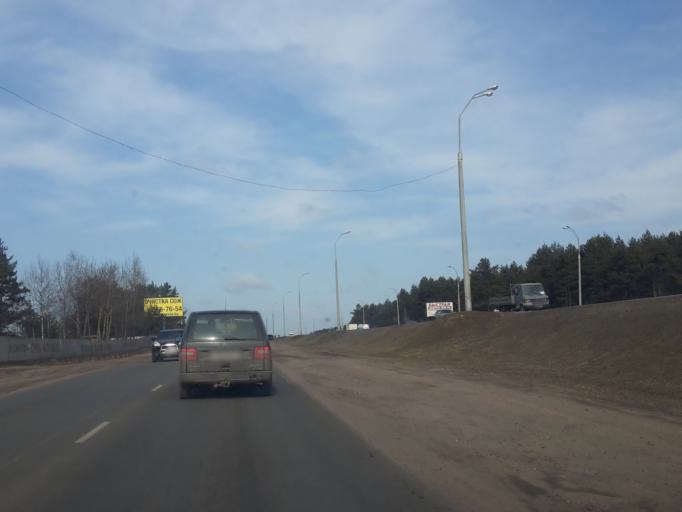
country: BY
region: Minsk
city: Vyaliki Trastsyanets
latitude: 53.9037
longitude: 27.6879
